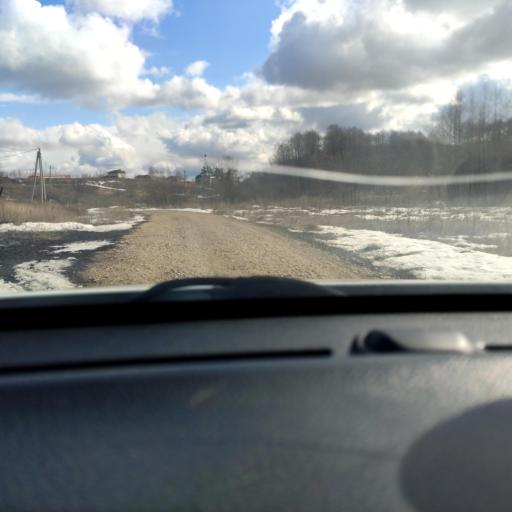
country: RU
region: Voronezj
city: Novaya Usman'
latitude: 51.6850
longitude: 39.3901
